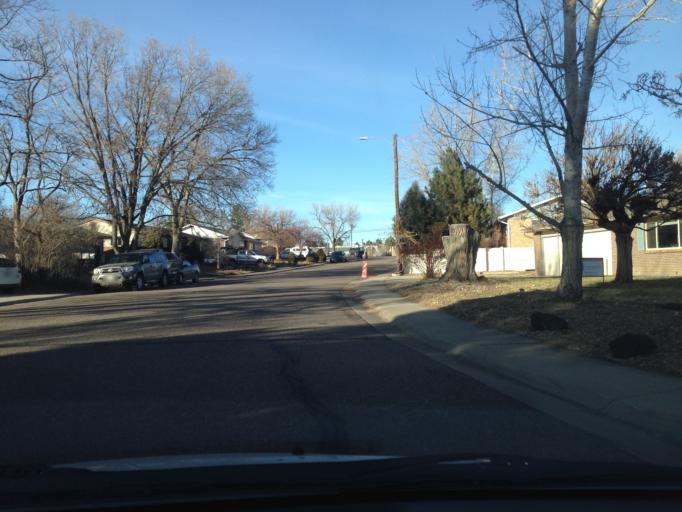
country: US
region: Colorado
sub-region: Boulder County
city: Louisville
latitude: 39.9857
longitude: -105.1348
